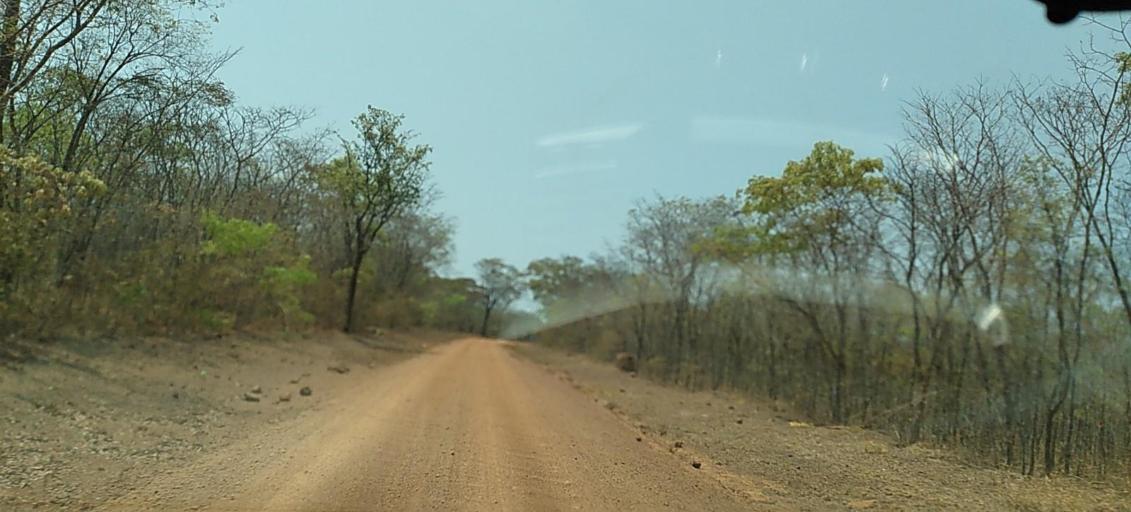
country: ZM
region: Central
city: Mumbwa
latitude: -14.2617
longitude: 26.5083
